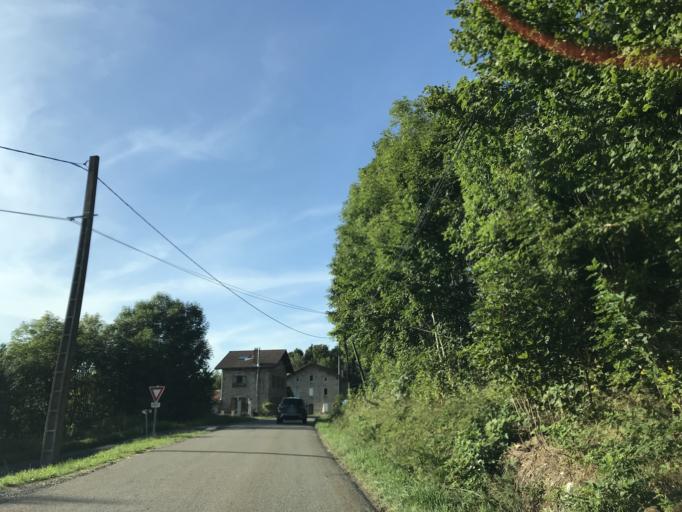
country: FR
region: Auvergne
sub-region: Departement du Puy-de-Dome
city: Job
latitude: 45.7052
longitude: 3.7211
